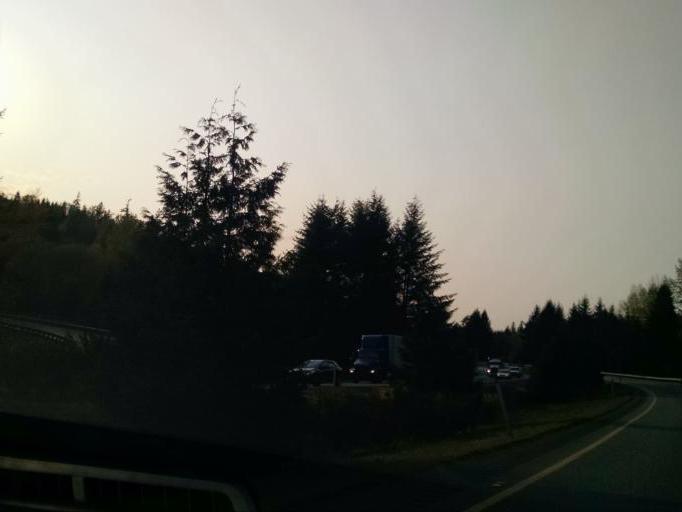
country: US
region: Washington
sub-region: Whatcom County
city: Geneva
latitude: 48.6856
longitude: -122.3947
